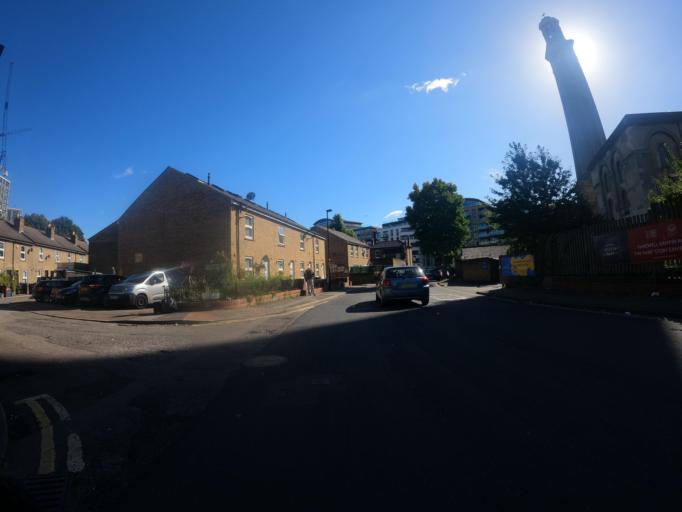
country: GB
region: England
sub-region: Greater London
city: Brentford
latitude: 51.4894
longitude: -0.2901
